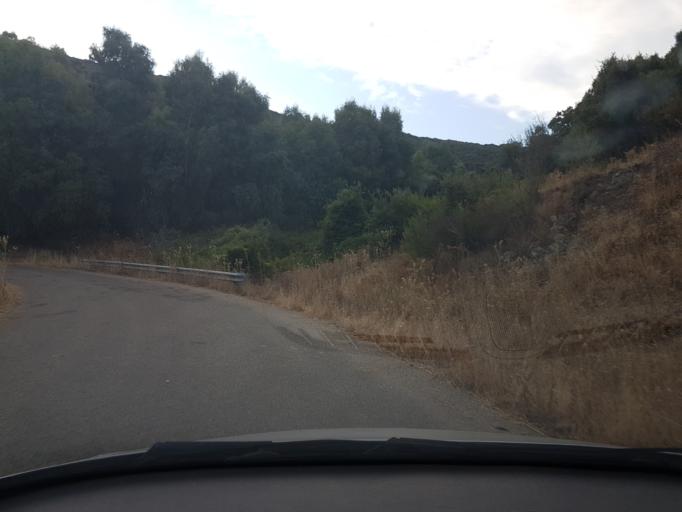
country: IT
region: Sardinia
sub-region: Provincia di Oristano
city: Seneghe
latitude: 40.1127
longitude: 8.6137
